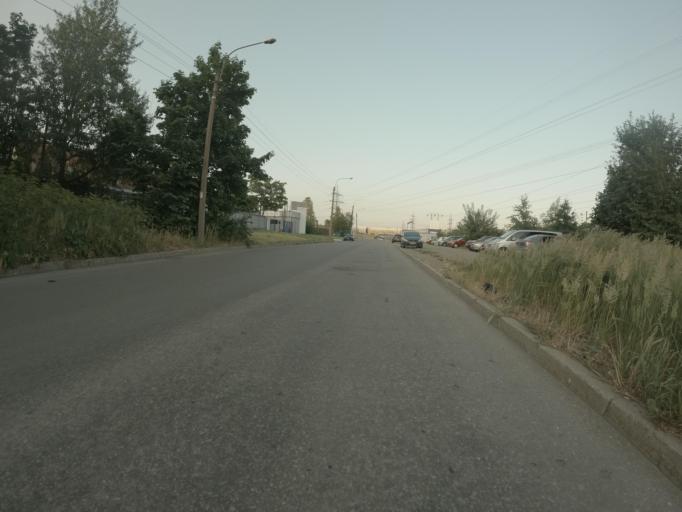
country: RU
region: St.-Petersburg
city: Krasnogvargeisky
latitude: 59.9756
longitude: 30.4412
